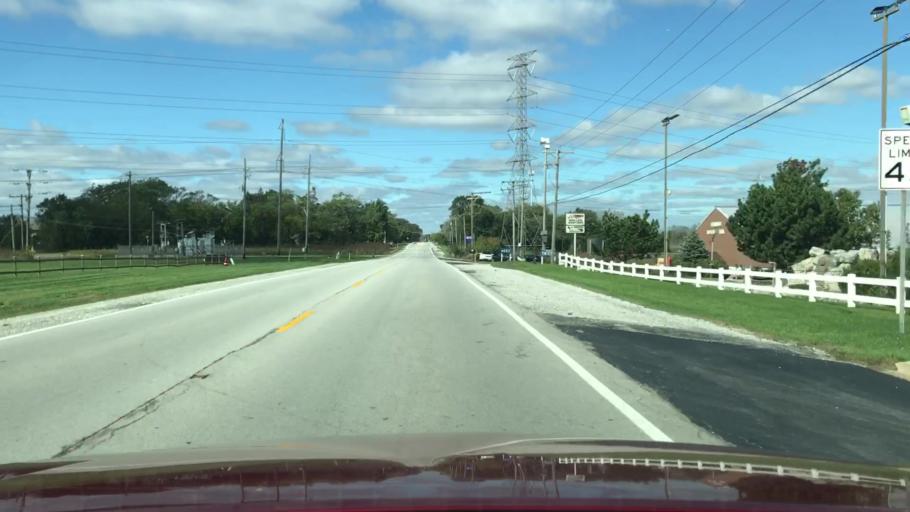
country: US
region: Illinois
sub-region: Cook County
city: Lynwood
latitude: 41.5267
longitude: -87.5660
